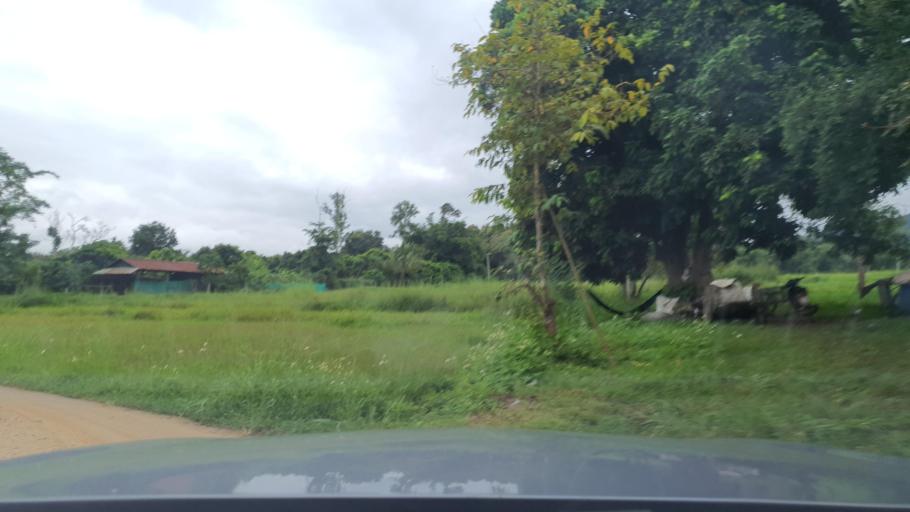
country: TH
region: Chiang Mai
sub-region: Amphoe Chiang Dao
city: Chiang Dao
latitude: 19.3320
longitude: 98.9348
